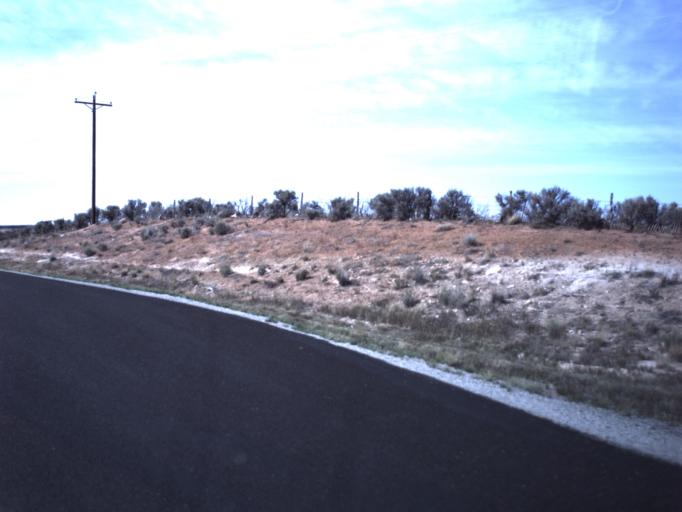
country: US
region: Colorado
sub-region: Dolores County
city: Dove Creek
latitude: 37.8171
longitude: -109.0441
